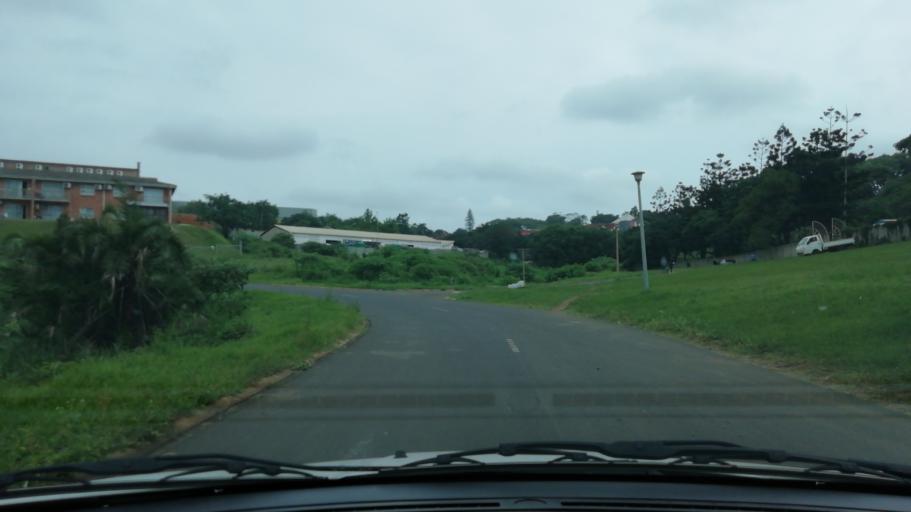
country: ZA
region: KwaZulu-Natal
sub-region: uThungulu District Municipality
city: Empangeni
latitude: -28.7413
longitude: 31.8856
